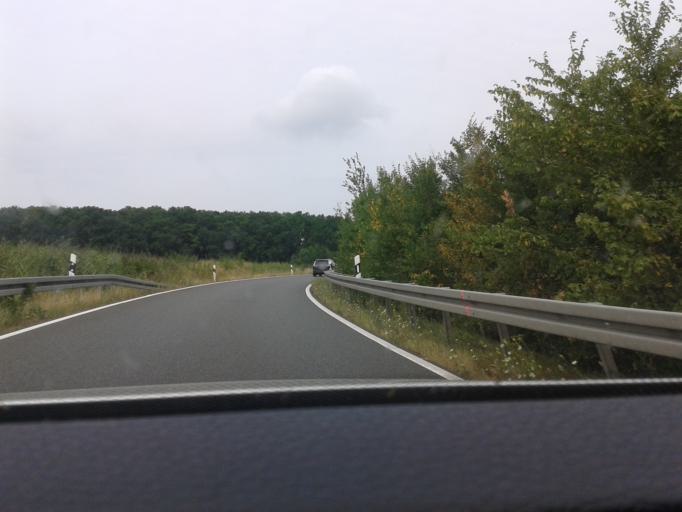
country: DE
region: Lower Saxony
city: Lehre
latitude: 52.3101
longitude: 10.7294
